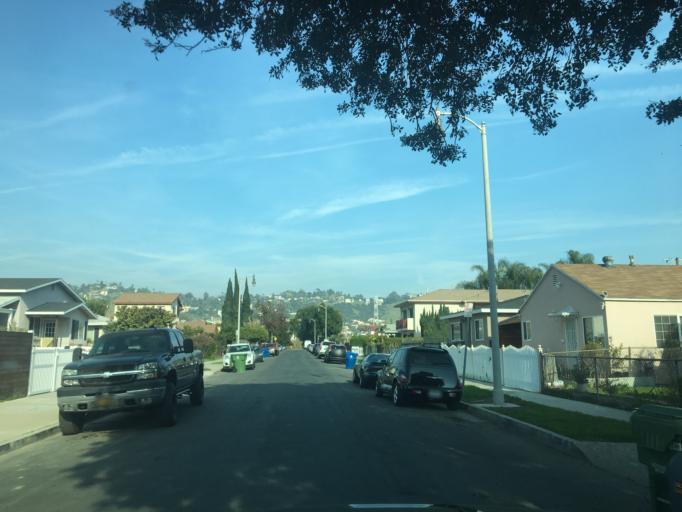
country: US
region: California
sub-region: Los Angeles County
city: Echo Park
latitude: 34.0890
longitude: -118.2330
